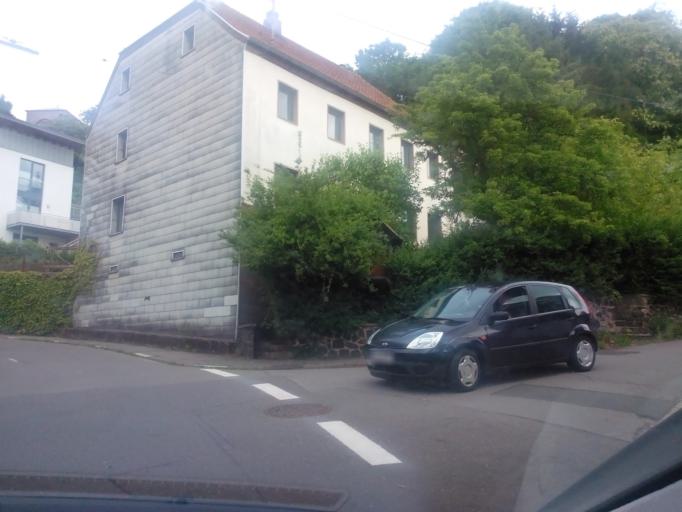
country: DE
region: Saarland
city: Eppelborn
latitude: 49.4189
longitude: 7.0113
